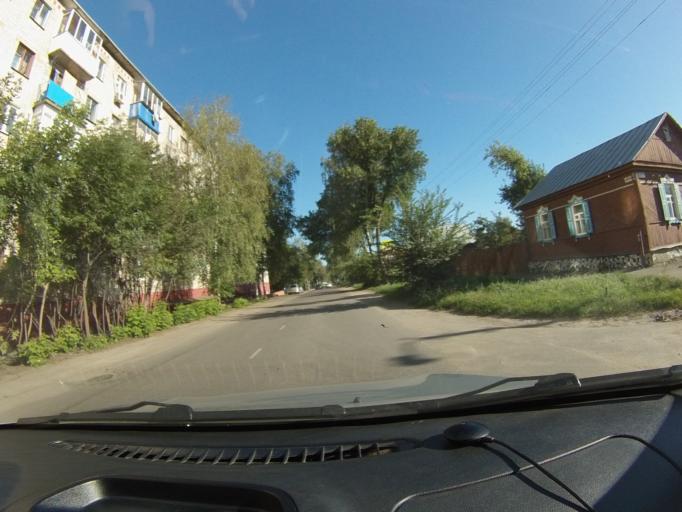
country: RU
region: Tambov
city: Tambov
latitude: 52.7581
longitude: 41.4223
